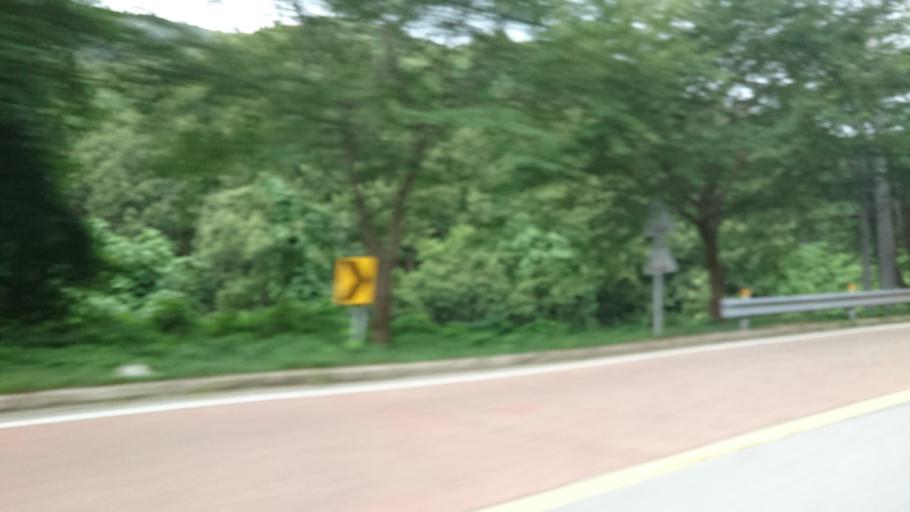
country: KR
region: Daegu
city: Daegu
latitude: 36.0216
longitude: 128.5625
